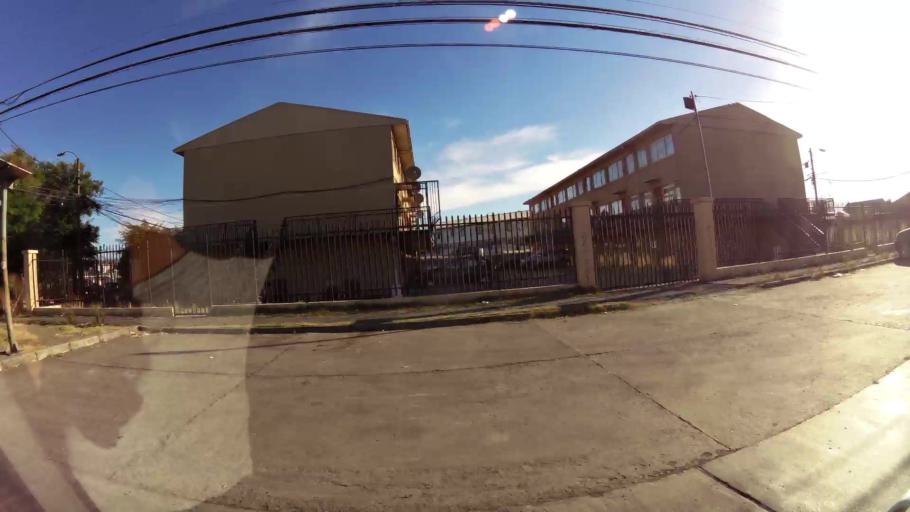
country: CL
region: Biobio
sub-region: Provincia de Concepcion
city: Concepcion
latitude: -36.8280
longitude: -73.1205
